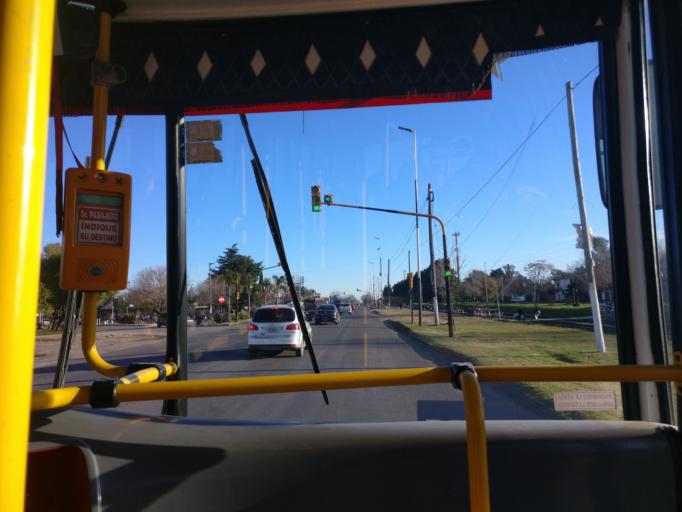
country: AR
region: Buenos Aires
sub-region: Partido de Ezeiza
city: Ezeiza
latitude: -34.8962
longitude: -58.5764
